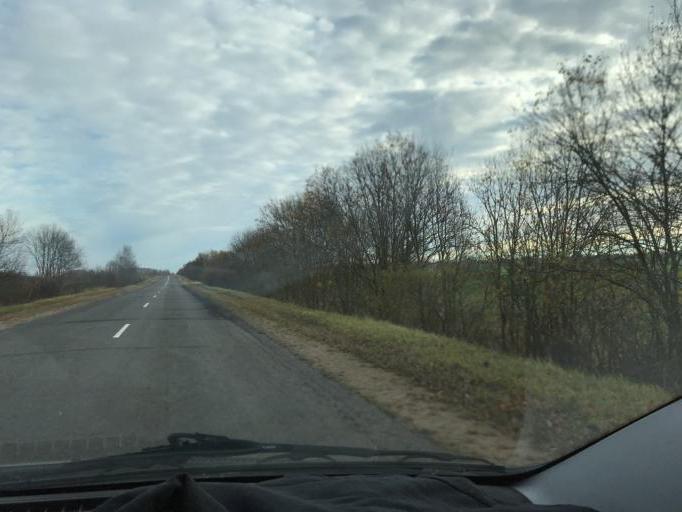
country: BY
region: Vitebsk
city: Haradok
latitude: 55.4093
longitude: 29.7497
